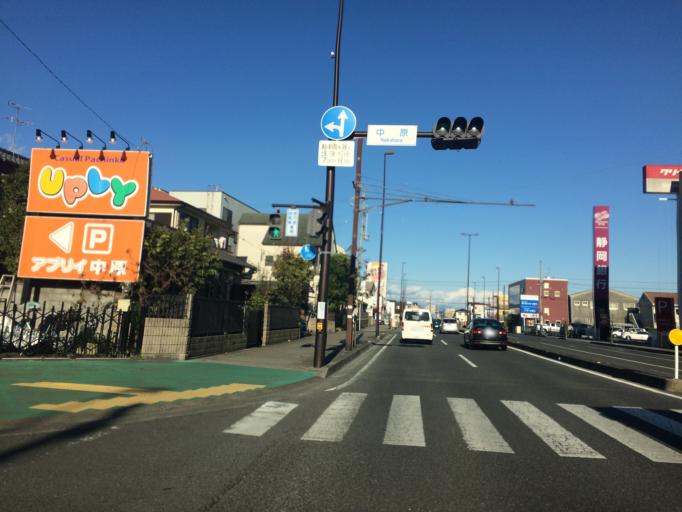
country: JP
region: Shizuoka
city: Shizuoka-shi
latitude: 34.9578
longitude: 138.3867
